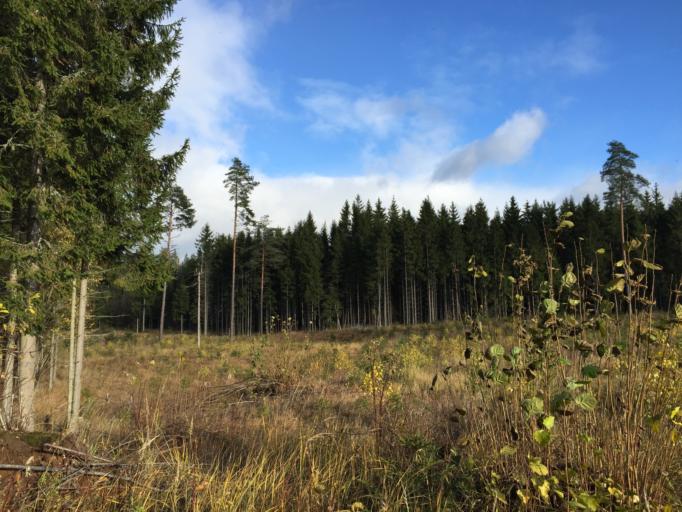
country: LV
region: Tukuma Rajons
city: Tukums
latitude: 57.0009
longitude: 23.0017
